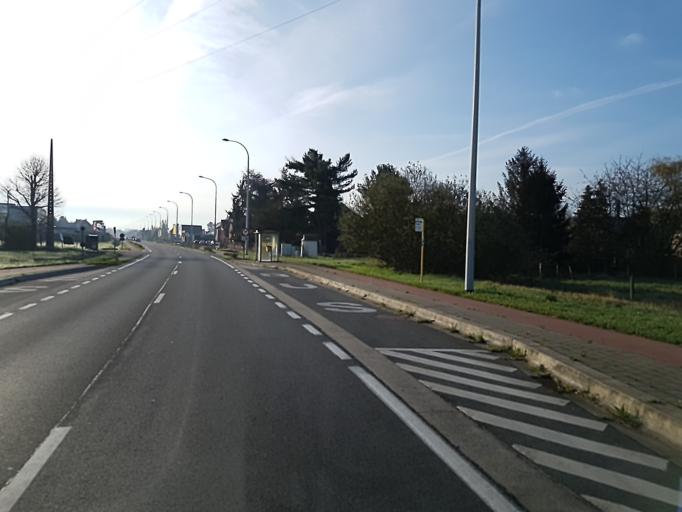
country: BE
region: Flanders
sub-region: Provincie Vlaams-Brabant
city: Aarschot
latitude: 51.0077
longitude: 4.8145
